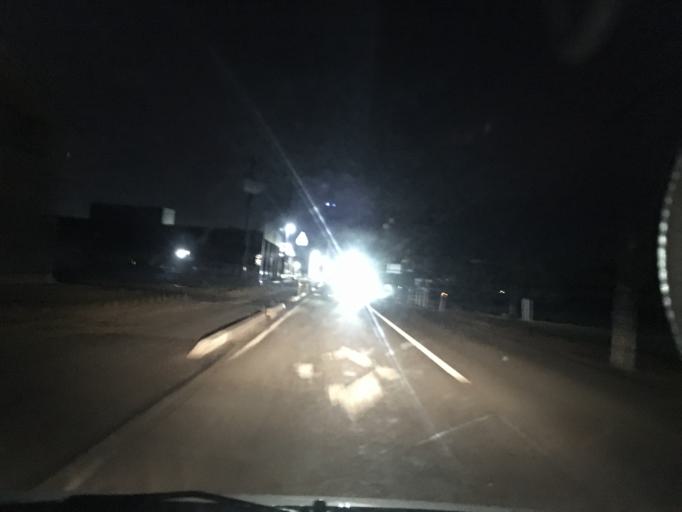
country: JP
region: Miyagi
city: Wakuya
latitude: 38.7053
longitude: 141.2218
